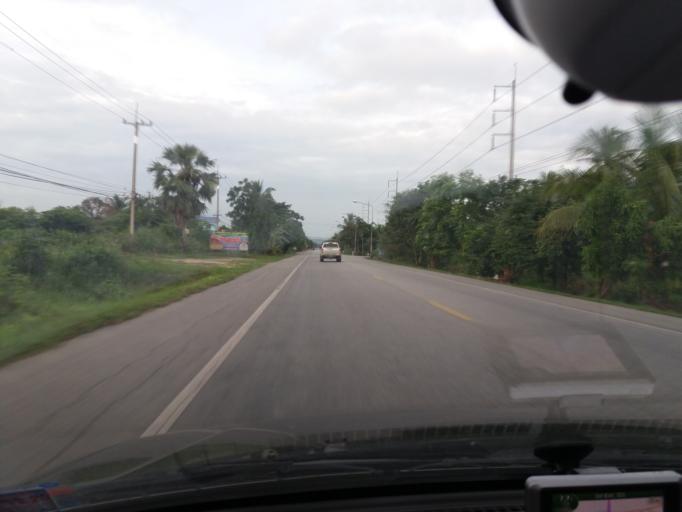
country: TH
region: Suphan Buri
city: U Thong
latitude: 14.4418
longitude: 99.9163
